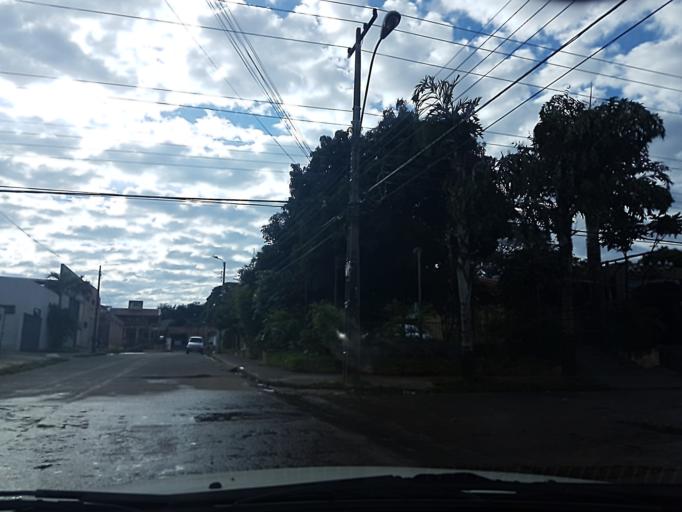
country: PY
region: Central
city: Lambare
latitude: -25.3312
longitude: -57.5911
